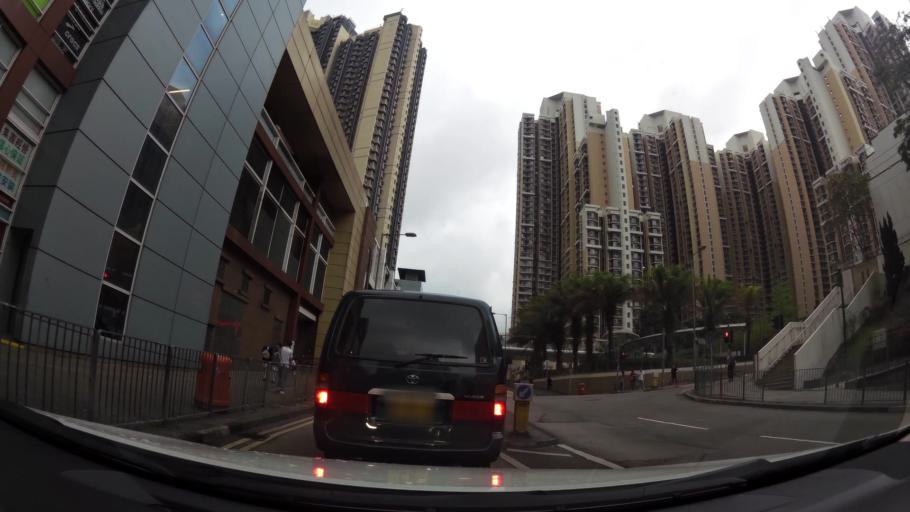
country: HK
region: Tsuen Wan
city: Tsuen Wan
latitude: 22.3681
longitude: 114.1281
